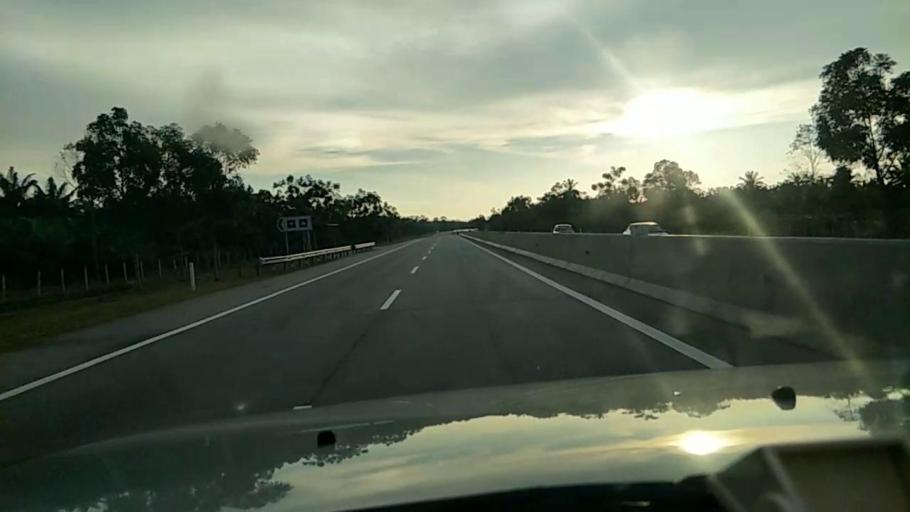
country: MY
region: Selangor
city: Batu Arang
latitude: 3.2881
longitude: 101.4244
